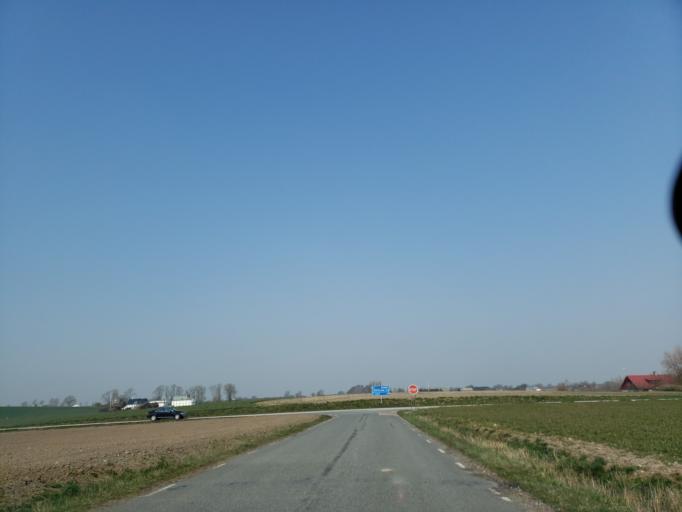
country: SE
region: Skane
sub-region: Simrishamns Kommun
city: Simrishamn
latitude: 55.4658
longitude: 14.2076
